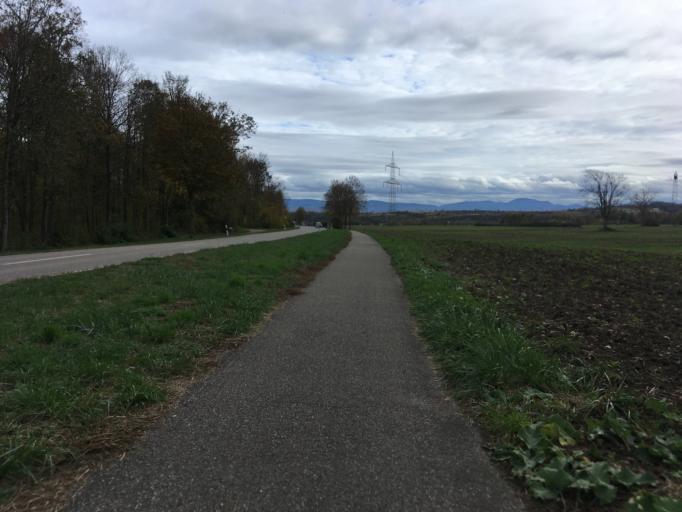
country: DE
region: Baden-Wuerttemberg
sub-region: Freiburg Region
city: Ihringen
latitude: 48.0287
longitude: 7.6621
